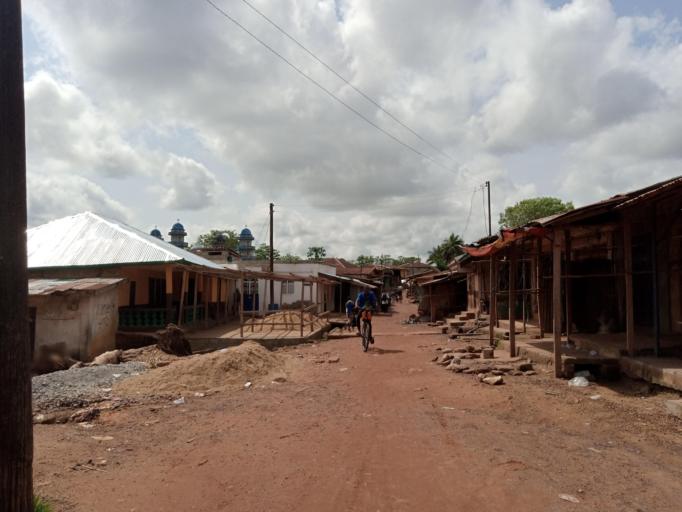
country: SL
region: Southern Province
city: Bo
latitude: 7.9639
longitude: -11.7369
